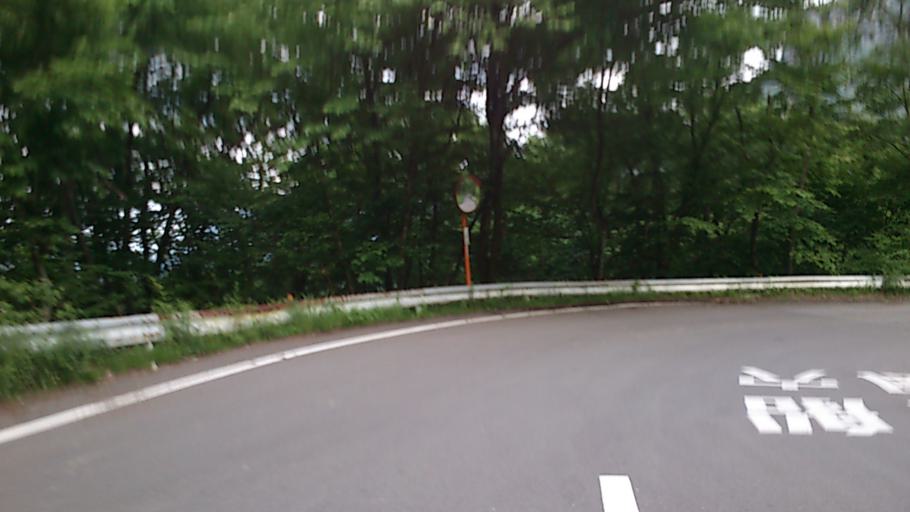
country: JP
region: Nagano
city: Saku
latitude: 36.2292
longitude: 138.6165
